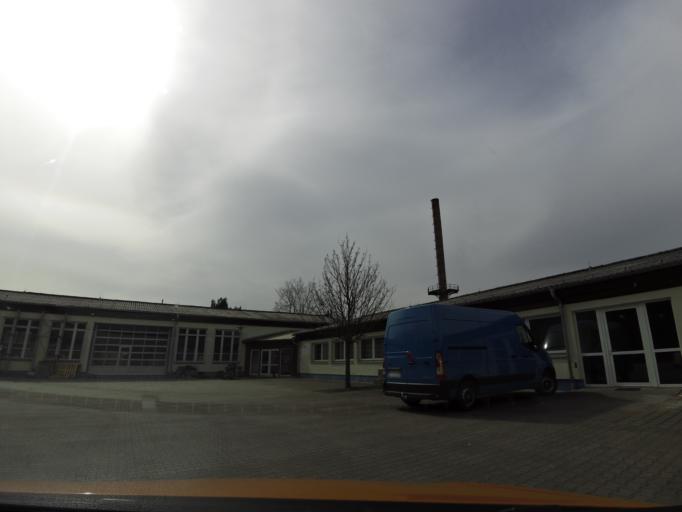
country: DE
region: Brandenburg
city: Rangsdorf
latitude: 52.3171
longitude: 13.3870
